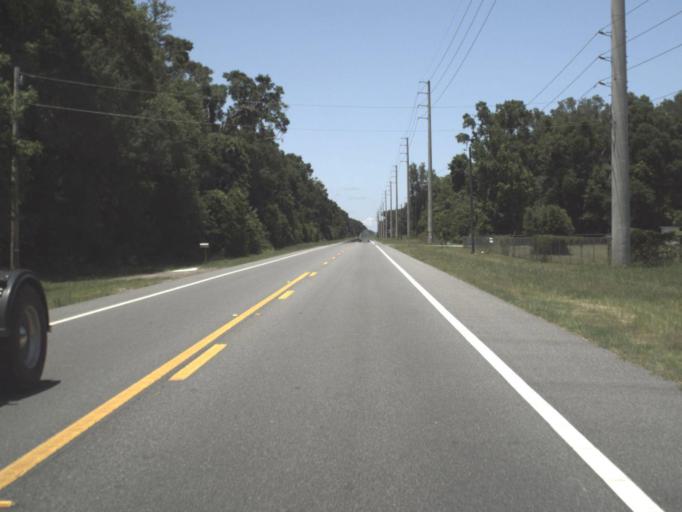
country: US
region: Florida
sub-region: Dixie County
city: Cross City
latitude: 29.6560
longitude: -82.9839
